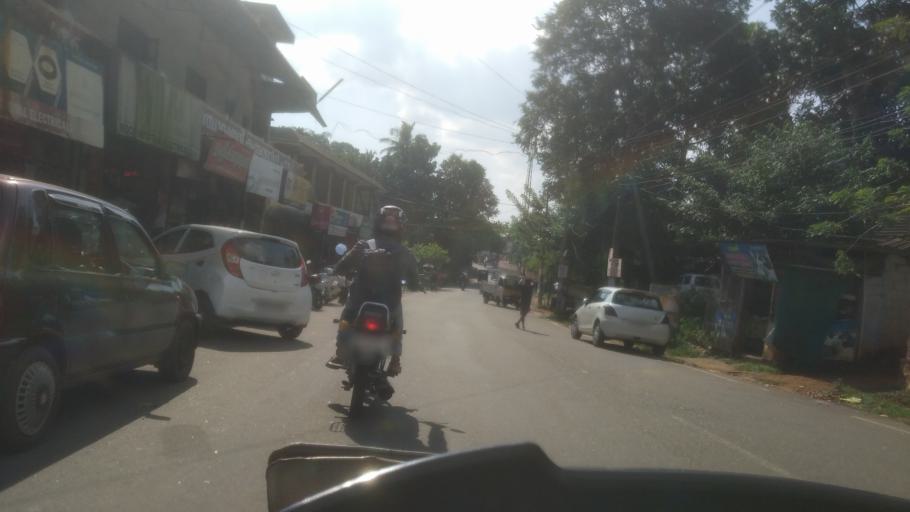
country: IN
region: Kerala
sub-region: Ernakulam
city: Kotamangalam
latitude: 10.0068
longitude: 76.7103
